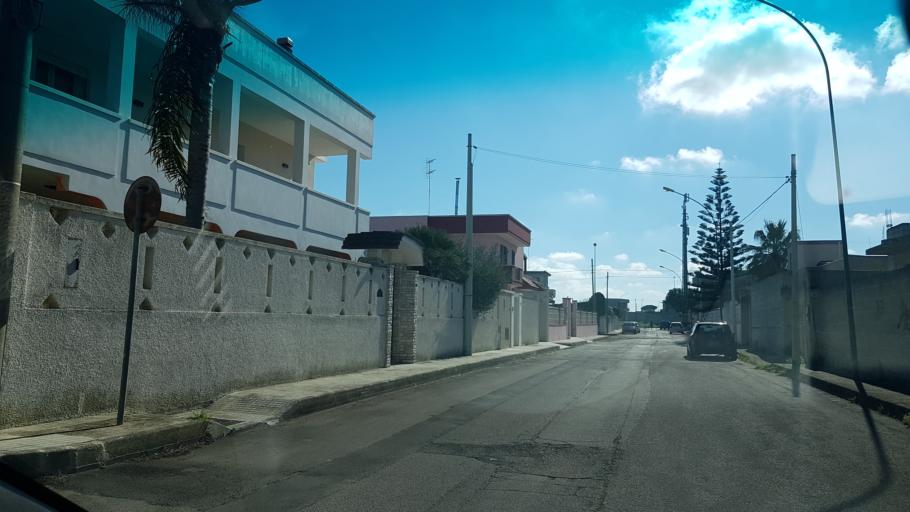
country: IT
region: Apulia
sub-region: Provincia di Lecce
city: Squinzano
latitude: 40.4371
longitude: 18.0509
